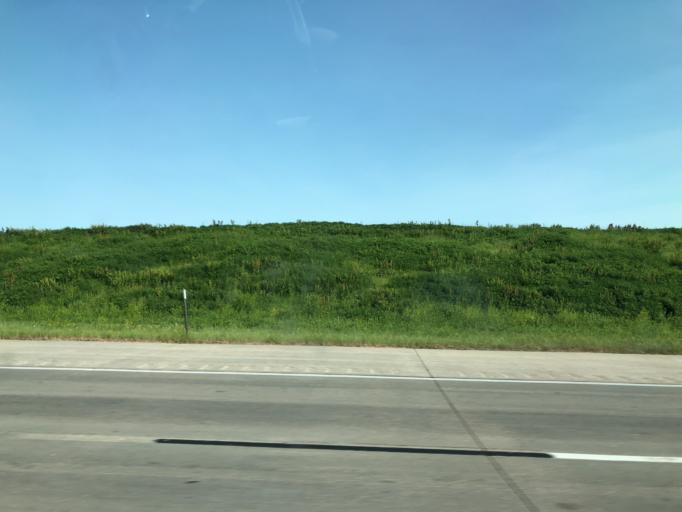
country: US
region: Nebraska
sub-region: Lancaster County
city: Waverly
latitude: 40.9174
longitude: -96.4721
